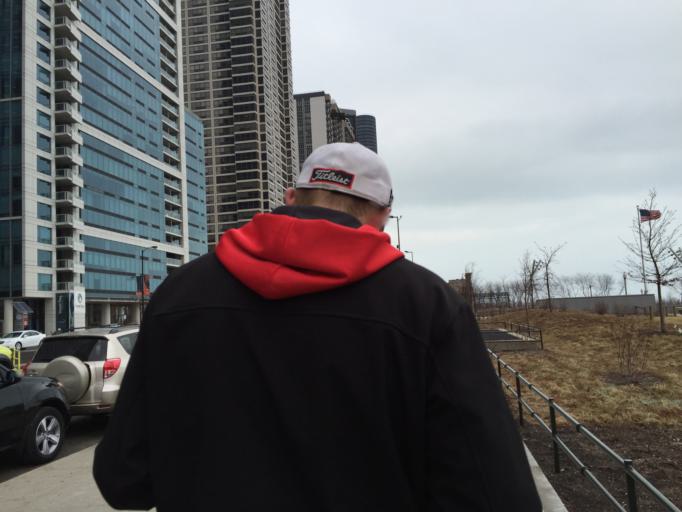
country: US
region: Illinois
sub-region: Cook County
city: Chicago
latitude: 41.8842
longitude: -87.6199
